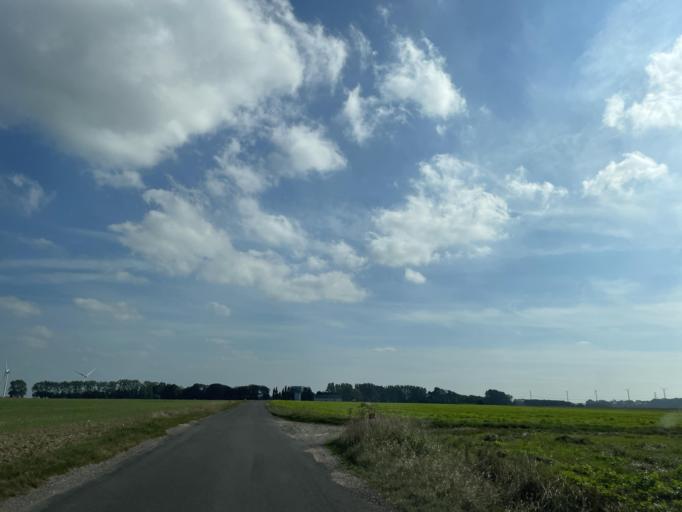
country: FR
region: Haute-Normandie
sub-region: Departement de la Seine-Maritime
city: Criel-sur-Mer
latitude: 50.0341
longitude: 1.3450
